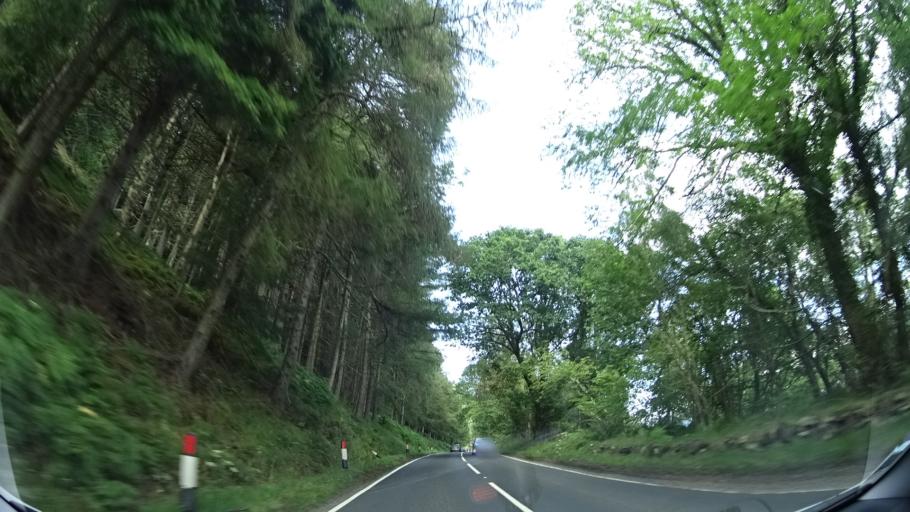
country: GB
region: Scotland
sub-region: Highland
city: Beauly
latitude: 57.2607
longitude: -4.5217
